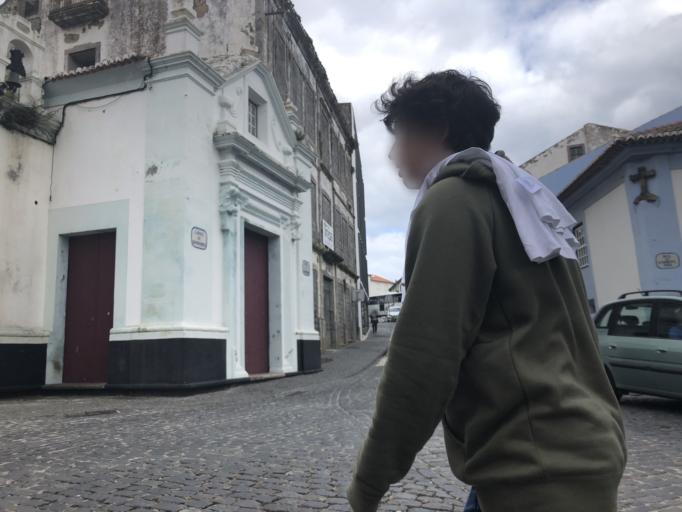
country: PT
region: Azores
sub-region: Angra do Heroismo
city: Angra do Heroismo
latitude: 38.6568
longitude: -27.2165
